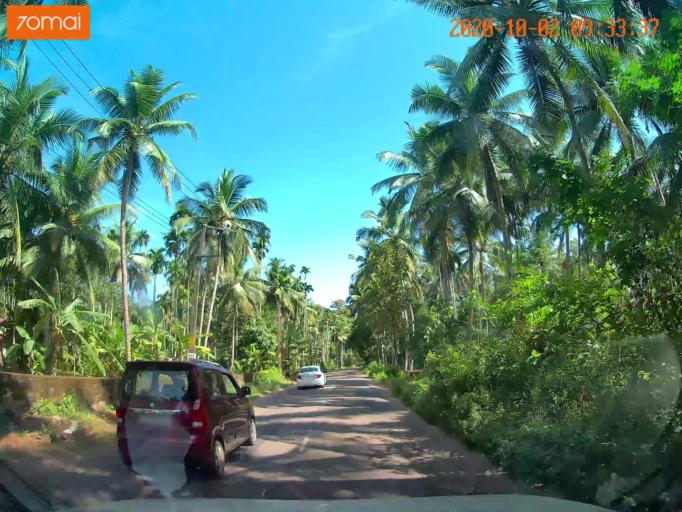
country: IN
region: Kerala
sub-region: Kozhikode
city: Nadapuram
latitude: 11.6325
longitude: 75.7517
